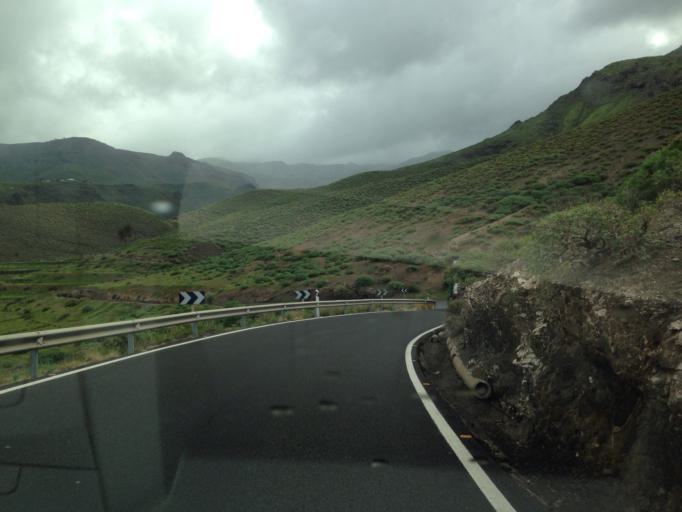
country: ES
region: Canary Islands
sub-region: Provincia de Las Palmas
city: Agaete
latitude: 28.0961
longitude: -15.7013
